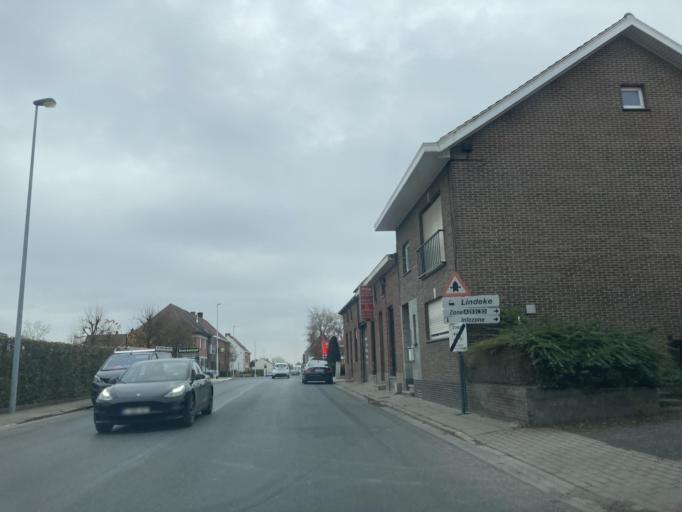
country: BE
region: Flanders
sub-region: Provincie West-Vlaanderen
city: Izegem
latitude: 50.8681
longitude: 3.1842
